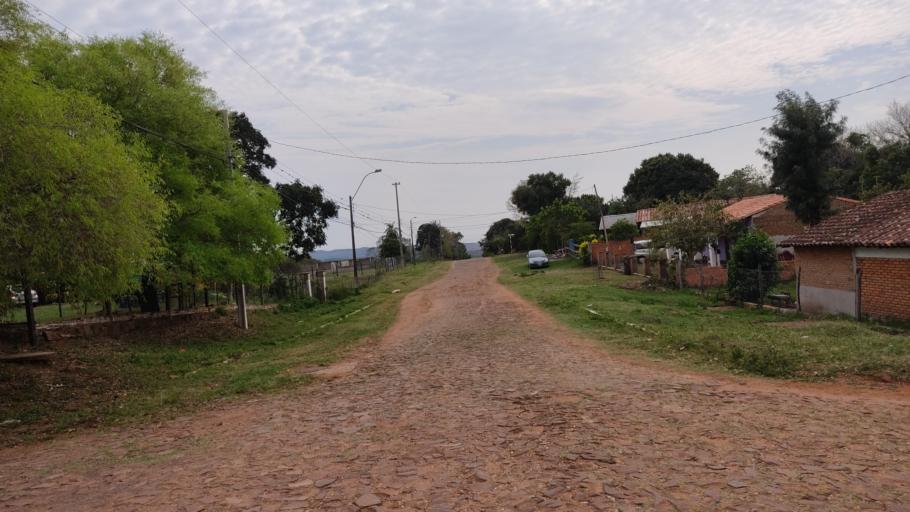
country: PY
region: Misiones
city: San Juan Bautista
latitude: -26.6626
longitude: -57.1513
